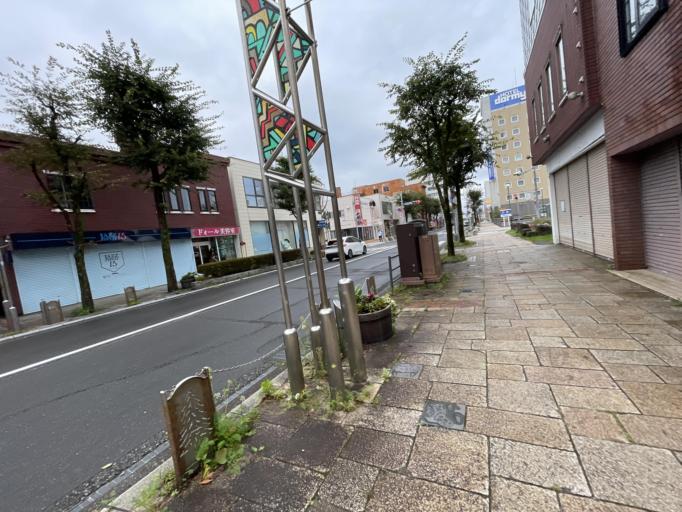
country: JP
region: Hokkaido
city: Tomakomai
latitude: 42.6345
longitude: 141.5994
